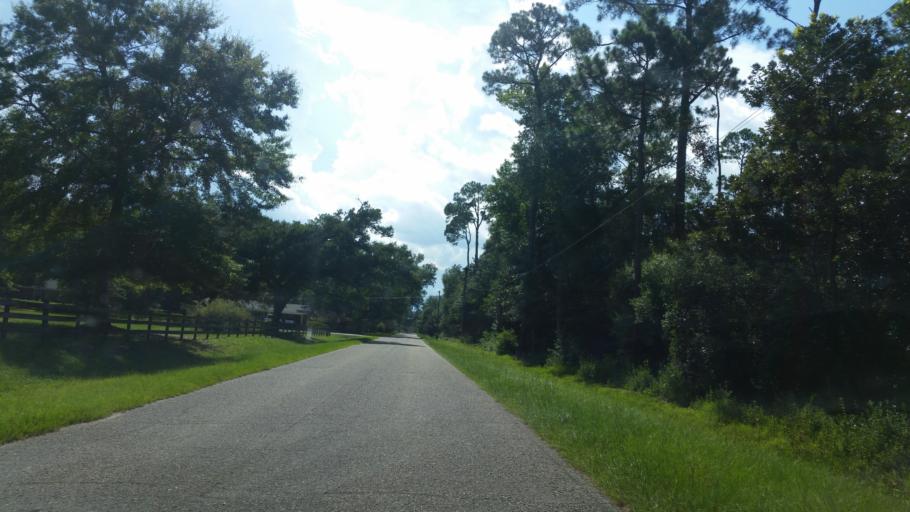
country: US
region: Florida
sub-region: Santa Rosa County
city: Pace
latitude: 30.5817
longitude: -87.1559
